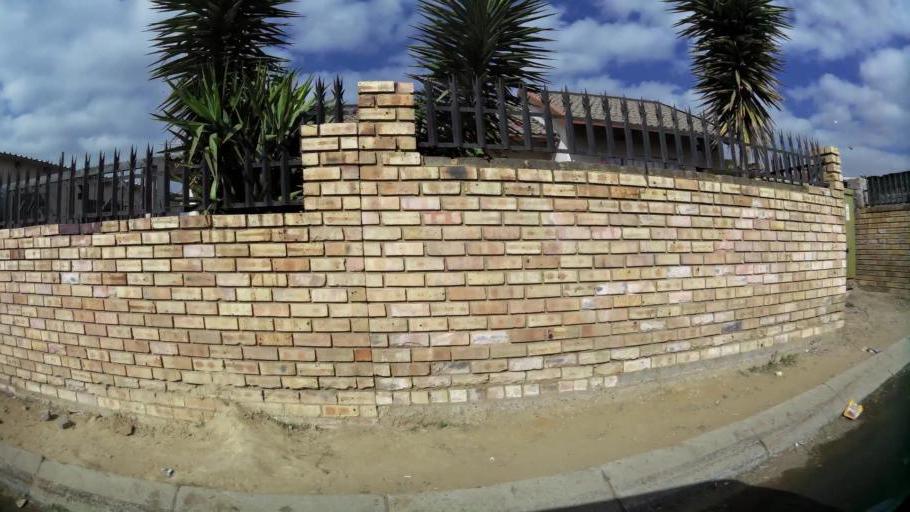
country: ZA
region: Gauteng
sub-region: City of Johannesburg Metropolitan Municipality
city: Roodepoort
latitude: -26.2146
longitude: 27.9093
